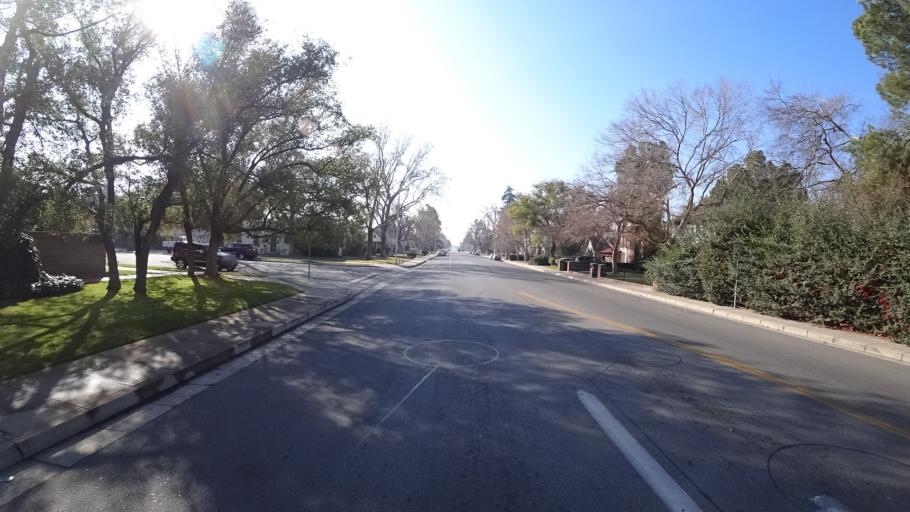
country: US
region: California
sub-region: Kern County
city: Bakersfield
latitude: 35.3901
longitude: -118.9949
